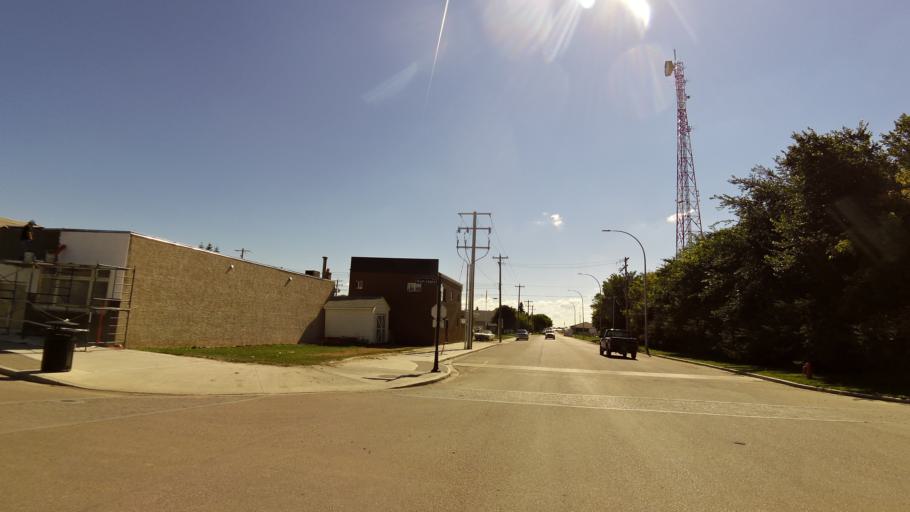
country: CA
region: Alberta
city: Wainwright
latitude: 52.8327
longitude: -110.8621
